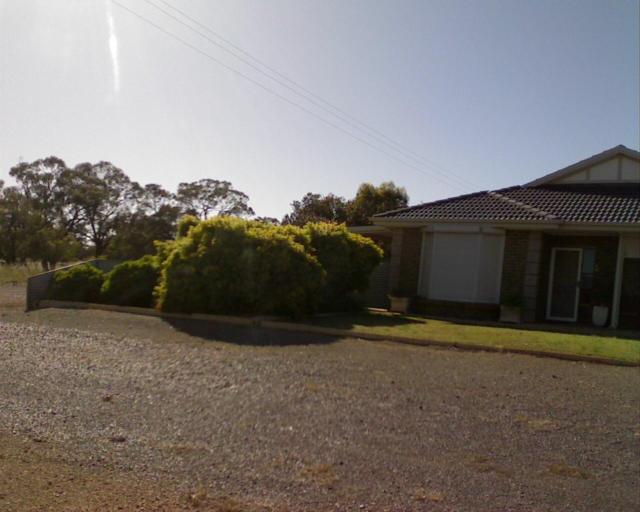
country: AU
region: South Australia
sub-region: Flinders Ranges
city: Quorn
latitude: -32.6479
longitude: 138.1025
